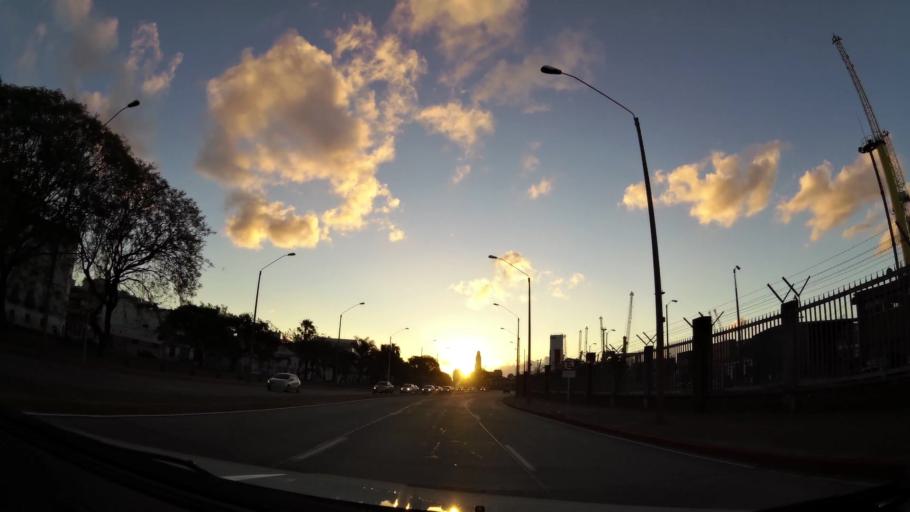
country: UY
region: Montevideo
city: Montevideo
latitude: -34.9020
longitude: -56.2036
